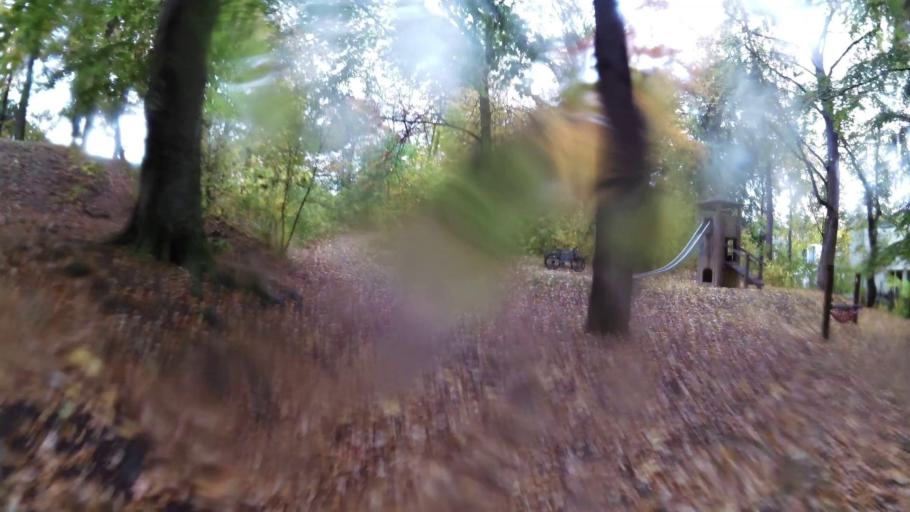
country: DE
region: Thuringia
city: Weimar
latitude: 50.9728
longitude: 11.3160
